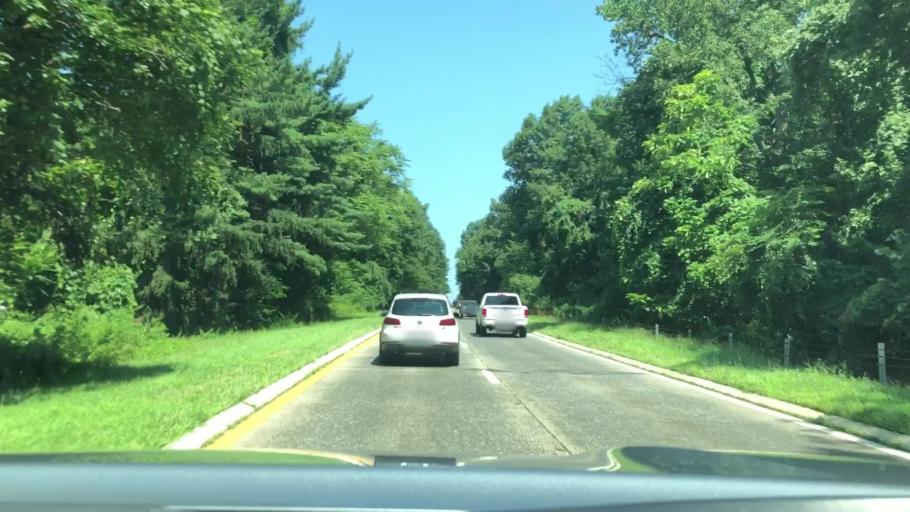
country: US
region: New York
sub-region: Rockland County
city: New Hempstead
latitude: 41.1539
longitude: -74.0265
